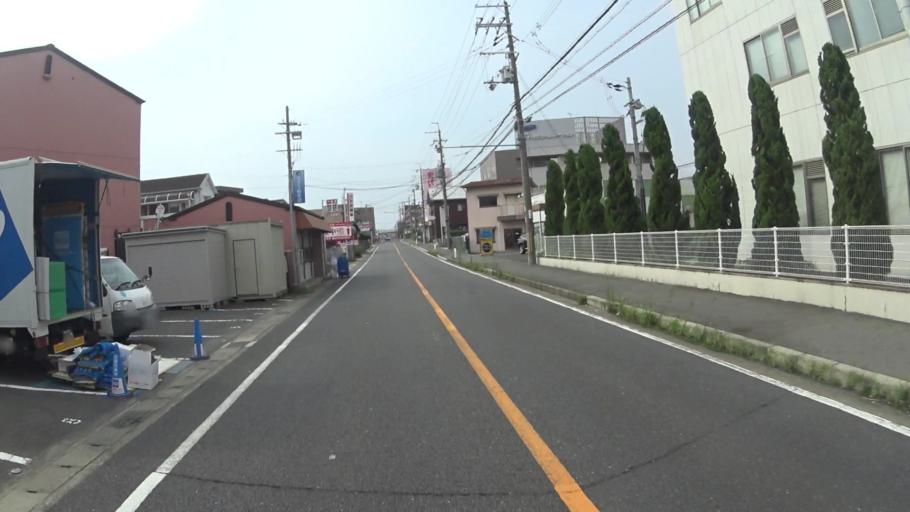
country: JP
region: Kyoto
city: Tanabe
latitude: 34.7752
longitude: 135.7894
